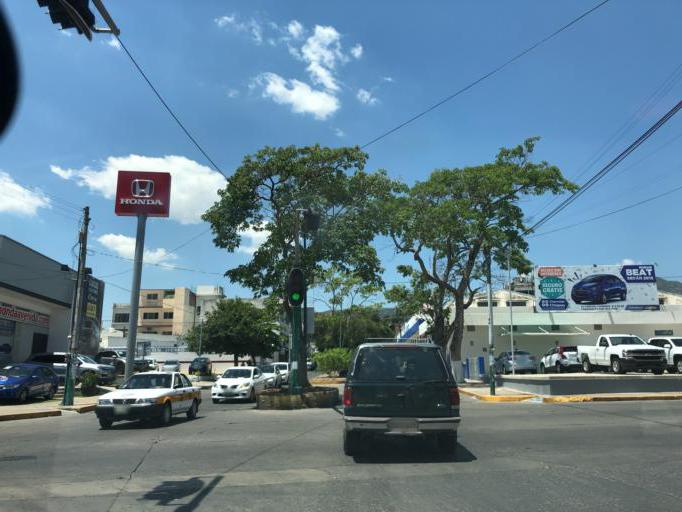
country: MX
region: Chiapas
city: Tuxtla Gutierrez
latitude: 16.7552
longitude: -93.1258
